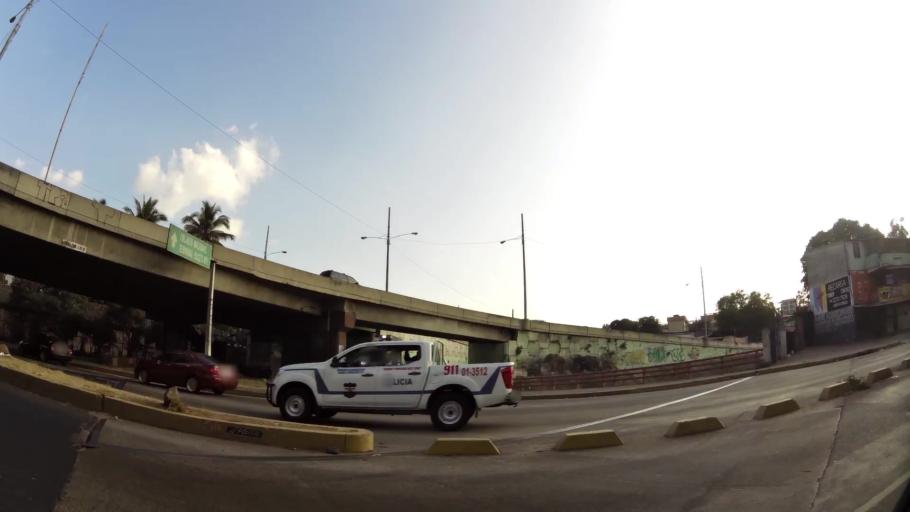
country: SV
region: San Salvador
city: San Salvador
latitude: 13.6923
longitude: -89.1924
